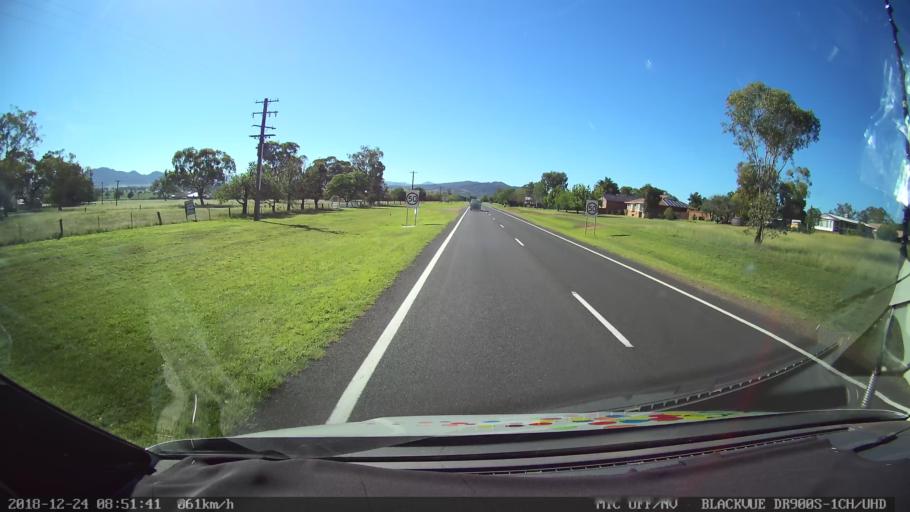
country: AU
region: New South Wales
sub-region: Liverpool Plains
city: Quirindi
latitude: -31.4866
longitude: 150.6756
